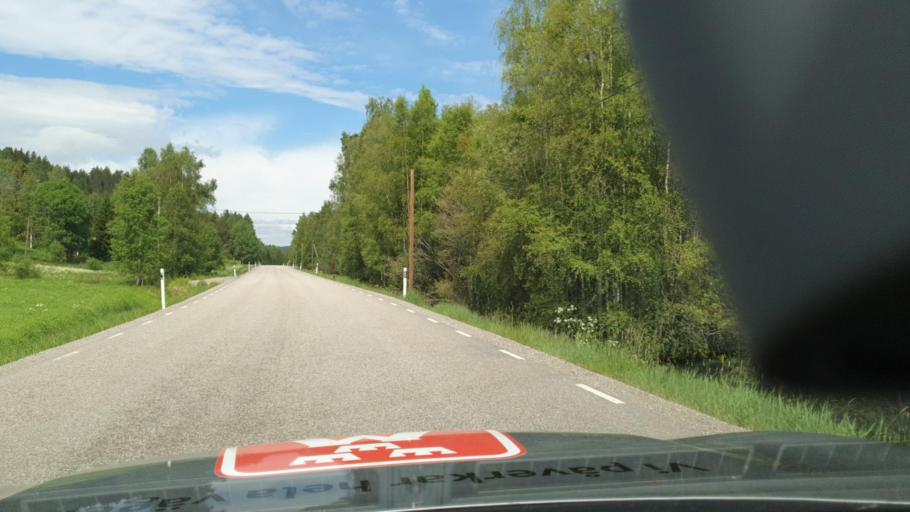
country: SE
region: Vaesternorrland
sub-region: Kramfors Kommun
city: Kramfors
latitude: 62.9477
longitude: 17.9046
